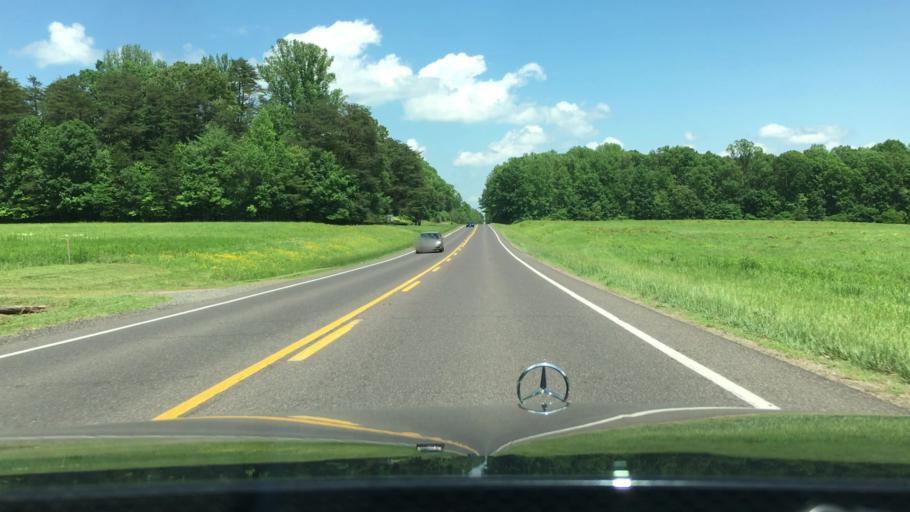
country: US
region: Virginia
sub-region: Spotsylvania County
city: Spotsylvania
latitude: 38.3163
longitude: -77.7563
